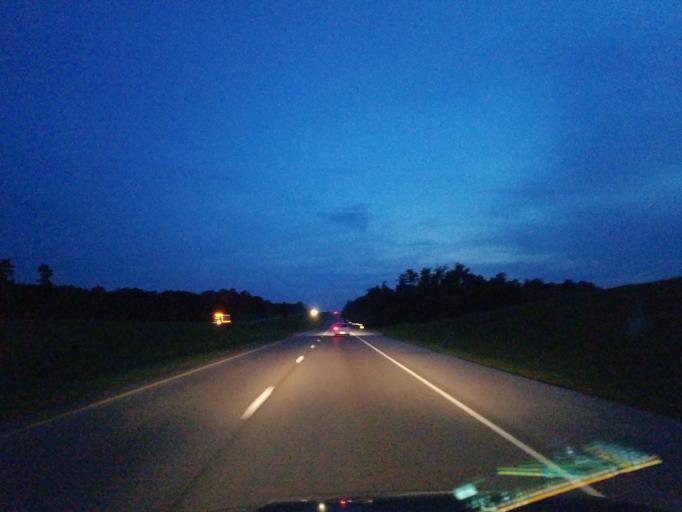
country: US
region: Mississippi
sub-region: Jones County
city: Ellisville
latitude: 31.5483
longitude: -89.2662
